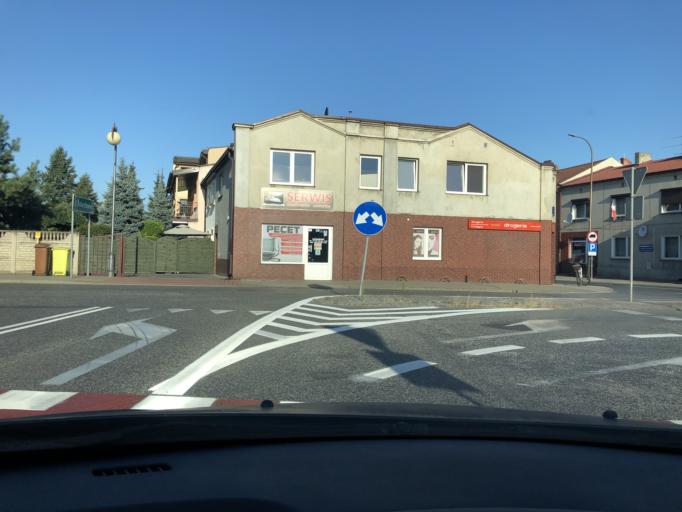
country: PL
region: Lodz Voivodeship
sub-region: Powiat wieruszowski
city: Wieruszow
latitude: 51.2944
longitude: 18.1569
